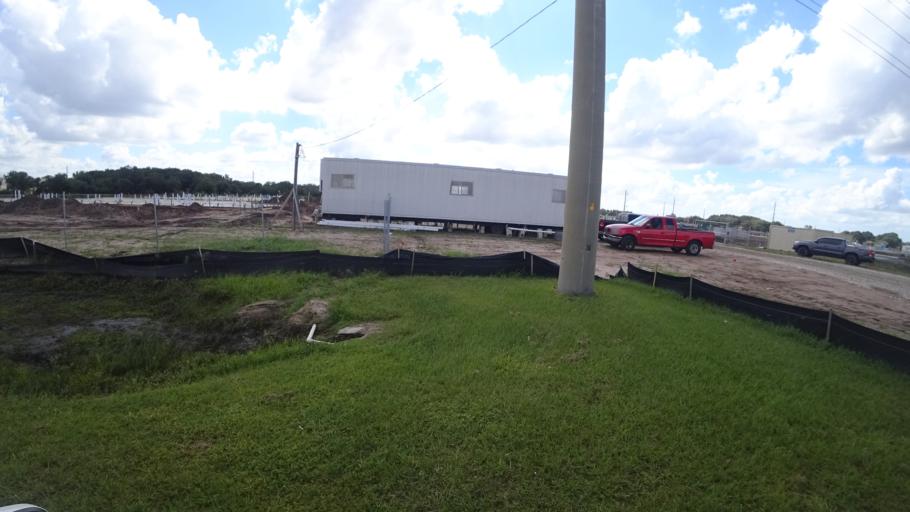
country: US
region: Florida
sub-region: Sarasota County
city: The Meadows
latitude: 27.4355
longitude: -82.3924
